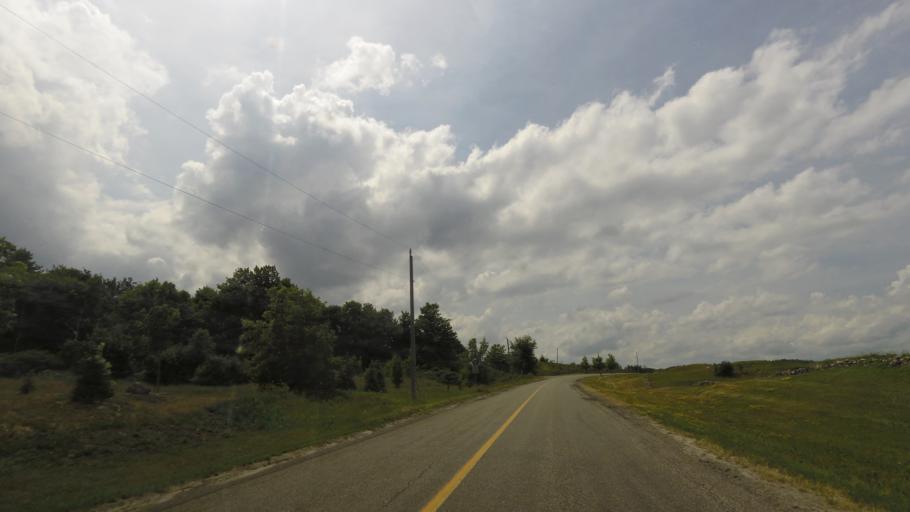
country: CA
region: Ontario
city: Orangeville
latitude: 43.8753
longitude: -79.9187
